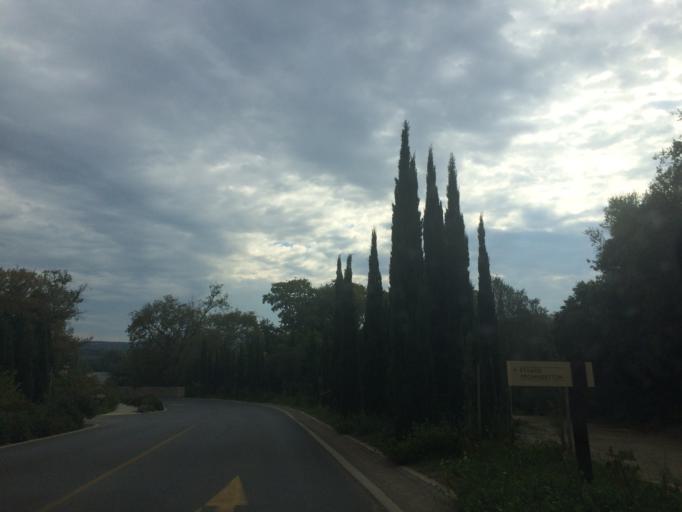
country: GR
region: Peloponnese
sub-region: Nomos Messinias
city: Gargalianoi
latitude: 36.9989
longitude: 21.6600
